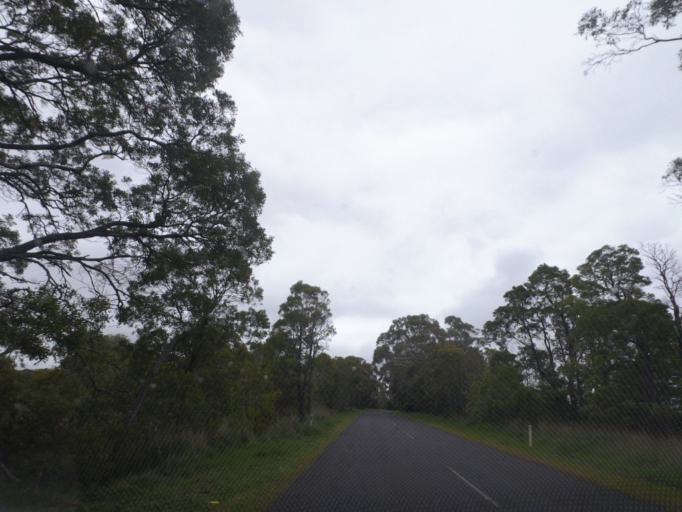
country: AU
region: Victoria
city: Brown Hill
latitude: -37.5957
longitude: 144.1608
